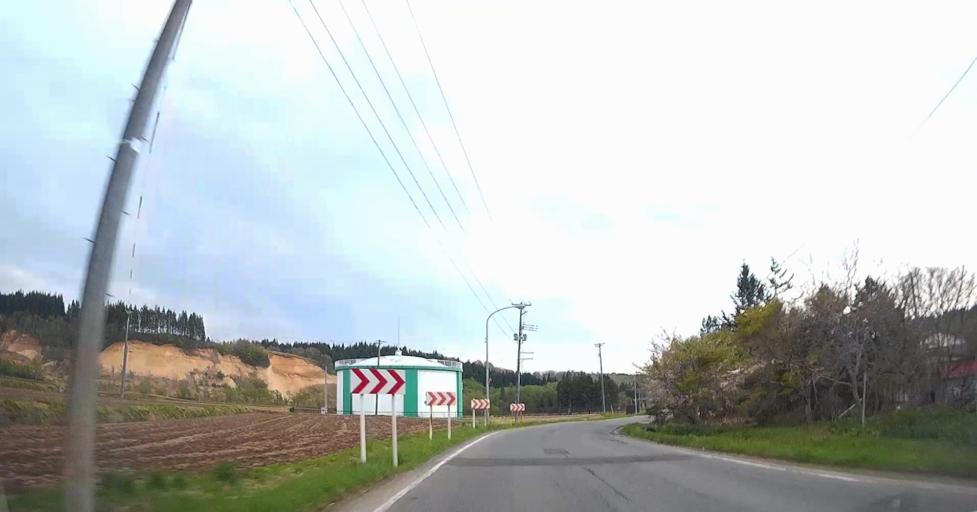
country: JP
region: Aomori
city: Goshogawara
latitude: 41.0897
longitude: 140.5530
